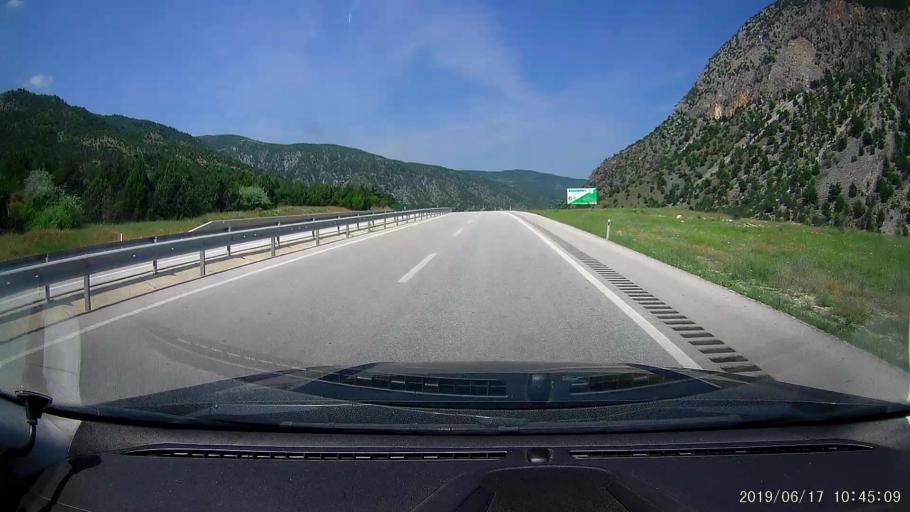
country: TR
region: Corum
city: Hacihamza
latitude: 41.0643
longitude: 34.4968
